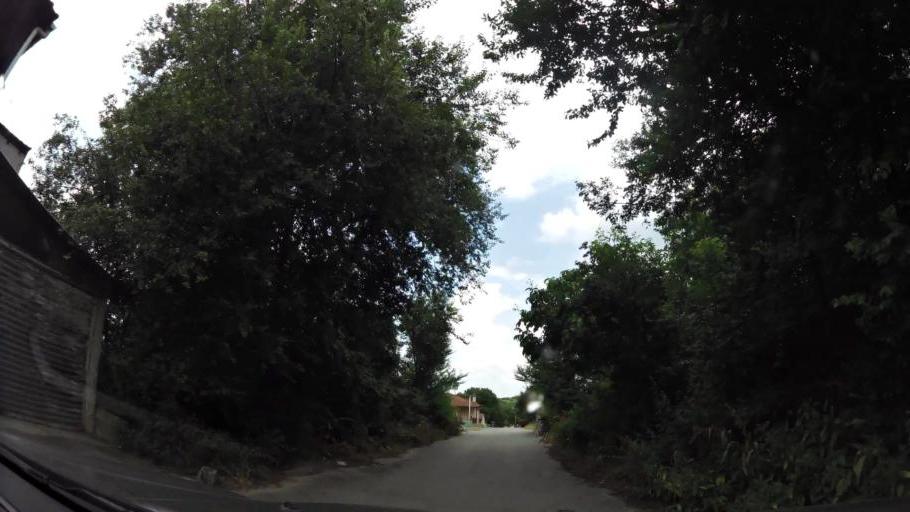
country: GR
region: West Macedonia
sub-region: Nomos Kozanis
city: Koila
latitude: 40.3463
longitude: 21.8285
